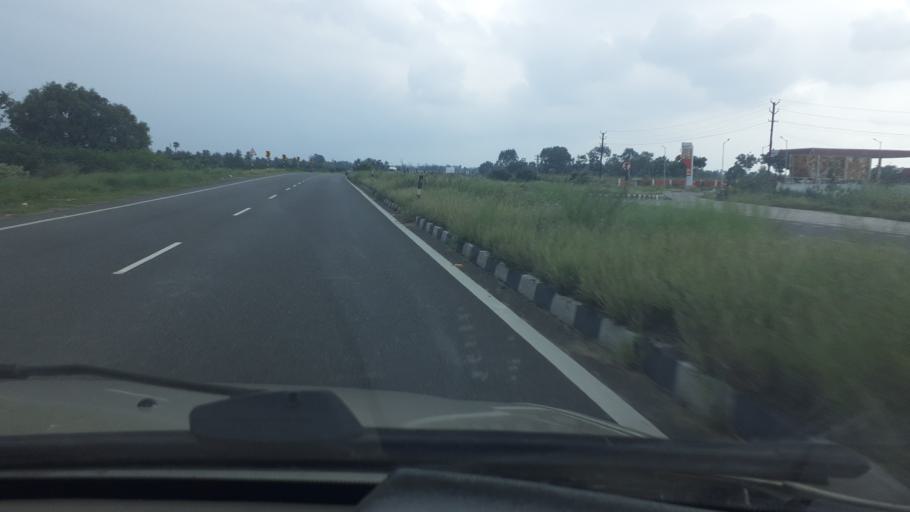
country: IN
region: Tamil Nadu
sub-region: Virudhunagar
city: Virudunagar
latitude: 9.6899
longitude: 77.9713
